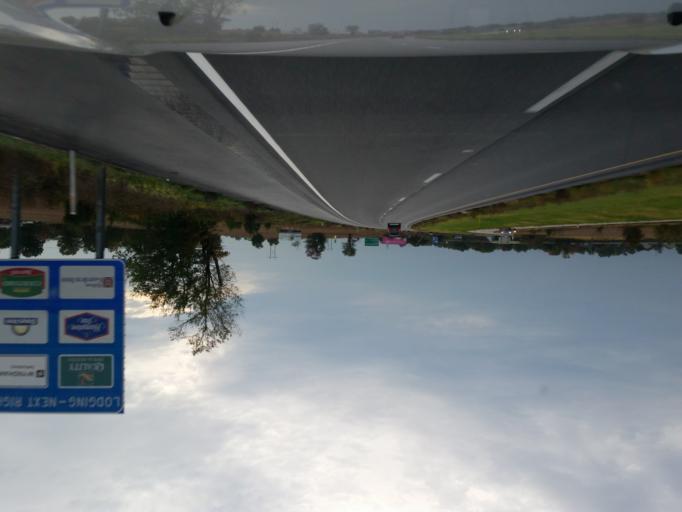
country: US
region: Pennsylvania
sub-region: Adams County
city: Gettysburg
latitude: 39.8650
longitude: -77.1968
